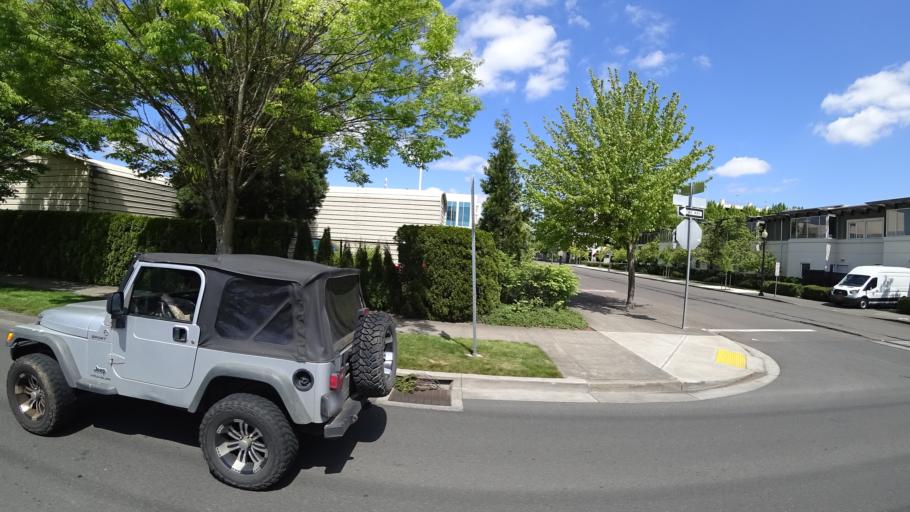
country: US
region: Oregon
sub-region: Washington County
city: Hillsboro
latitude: 45.5201
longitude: -122.9914
